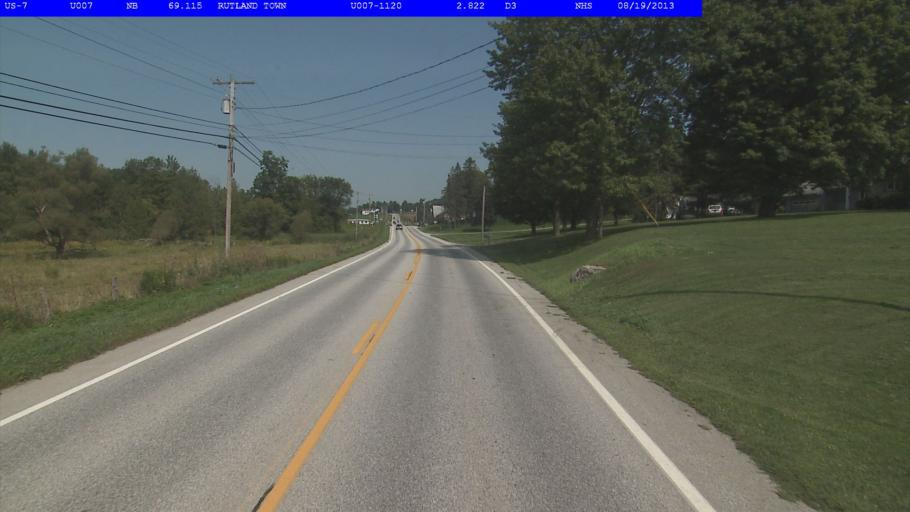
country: US
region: Vermont
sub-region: Rutland County
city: Rutland
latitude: 43.6513
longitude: -72.9857
